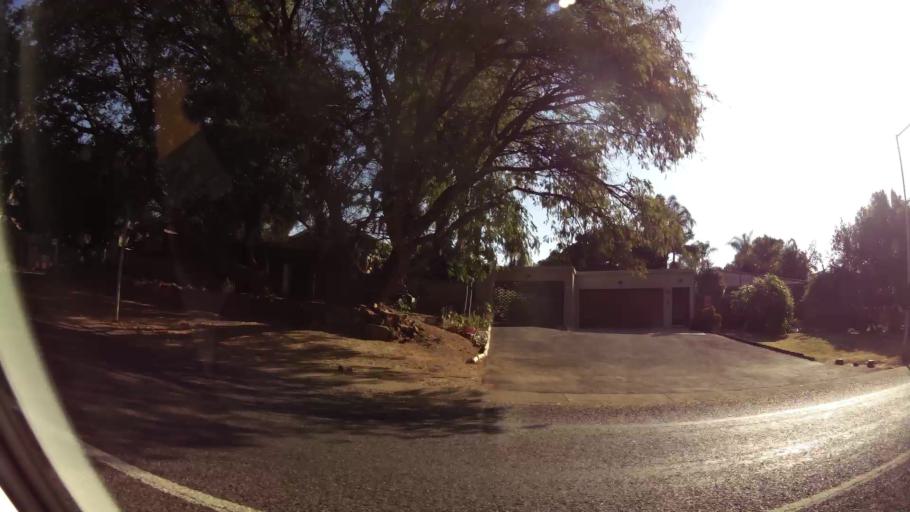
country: ZA
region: Gauteng
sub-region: City of Tshwane Metropolitan Municipality
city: Centurion
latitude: -25.8250
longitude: 28.2952
